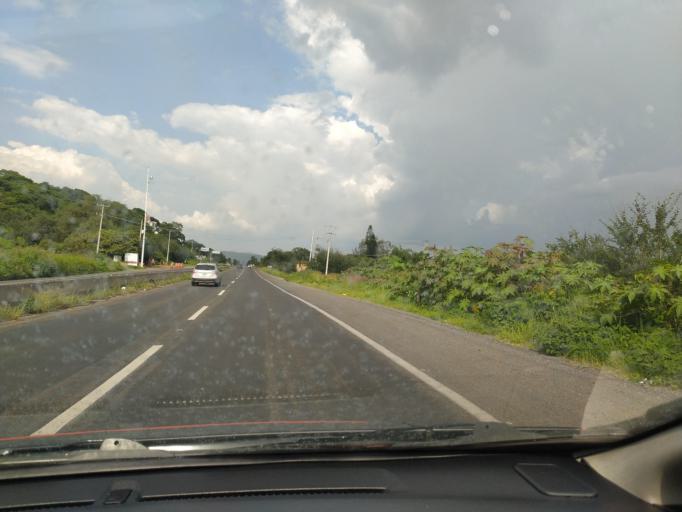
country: MX
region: Jalisco
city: Villa Corona
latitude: 20.4082
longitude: -103.6500
